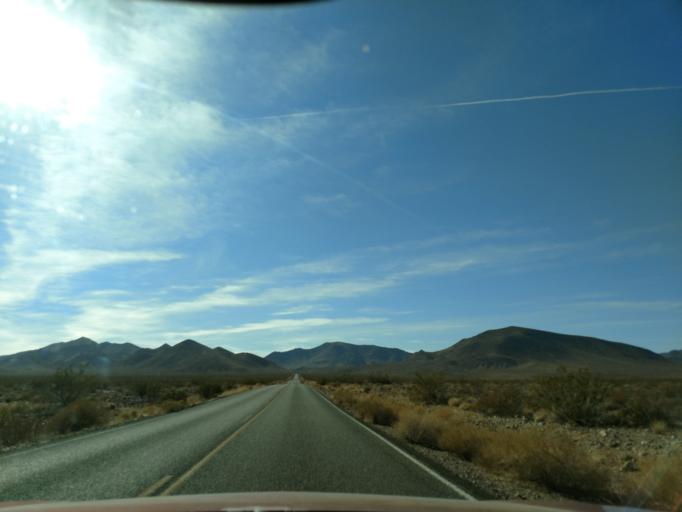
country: US
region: Nevada
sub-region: Nye County
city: Beatty
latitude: 36.8233
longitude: -116.8918
